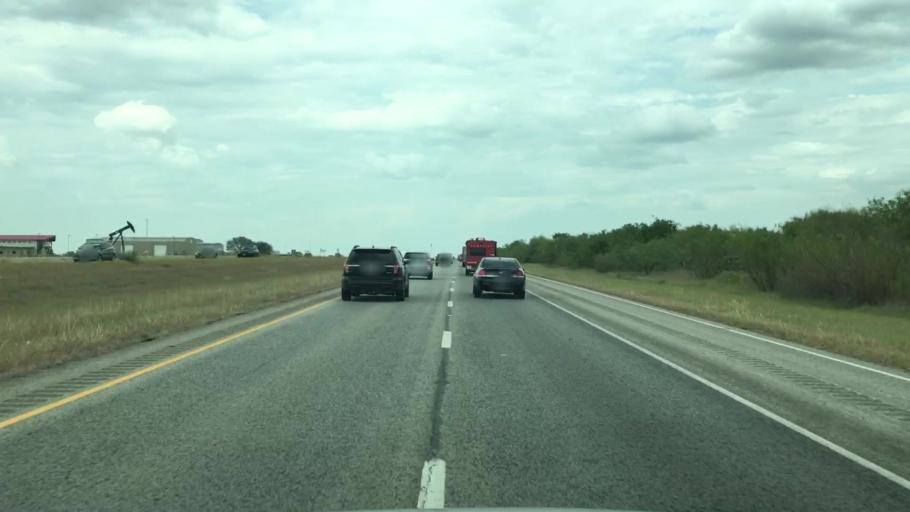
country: US
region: Texas
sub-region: Atascosa County
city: Pleasanton
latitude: 29.0955
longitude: -98.4327
